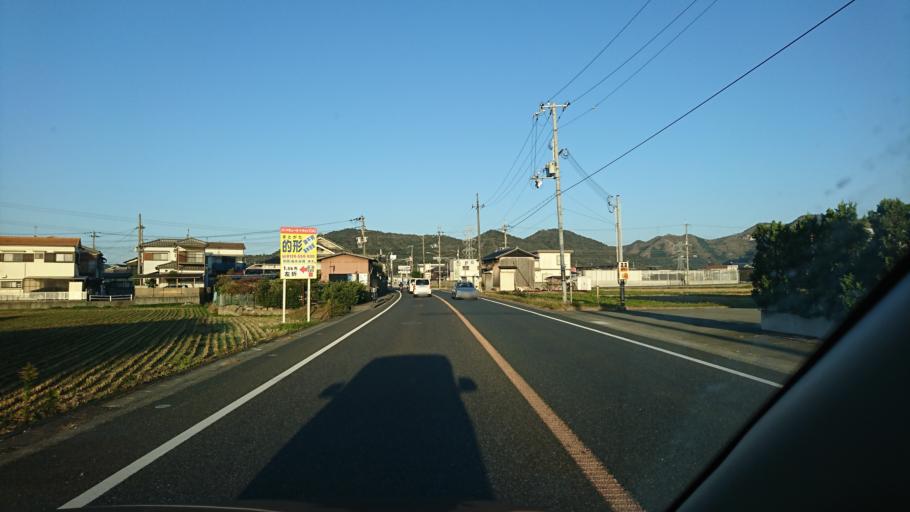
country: JP
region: Hyogo
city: Kakogawacho-honmachi
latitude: 34.7941
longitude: 134.7881
